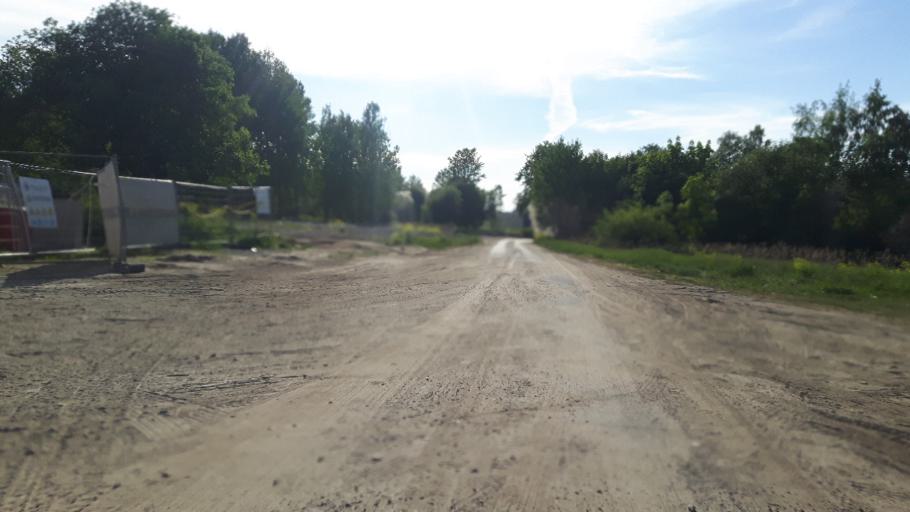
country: EE
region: Harju
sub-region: Tallinna linn
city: Kose
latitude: 59.4503
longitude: 24.8998
